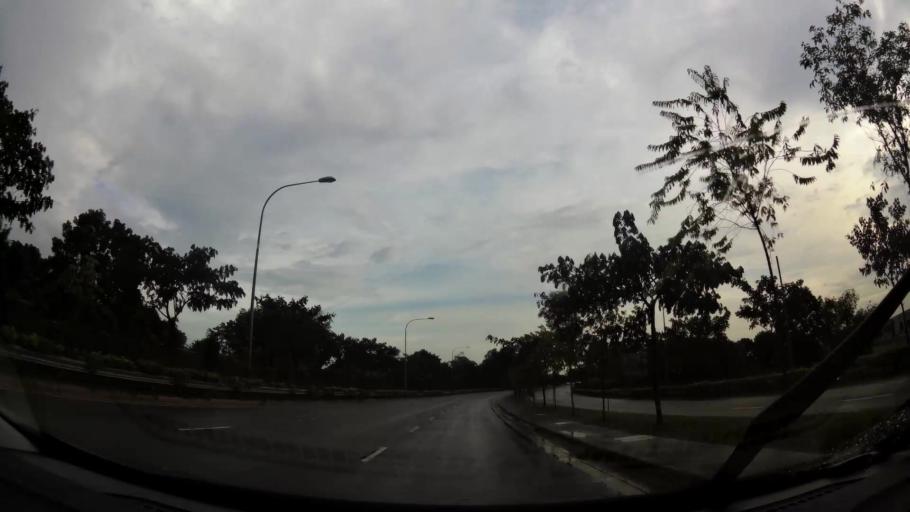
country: MY
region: Johor
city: Kampung Pasir Gudang Baru
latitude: 1.4055
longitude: 103.8686
